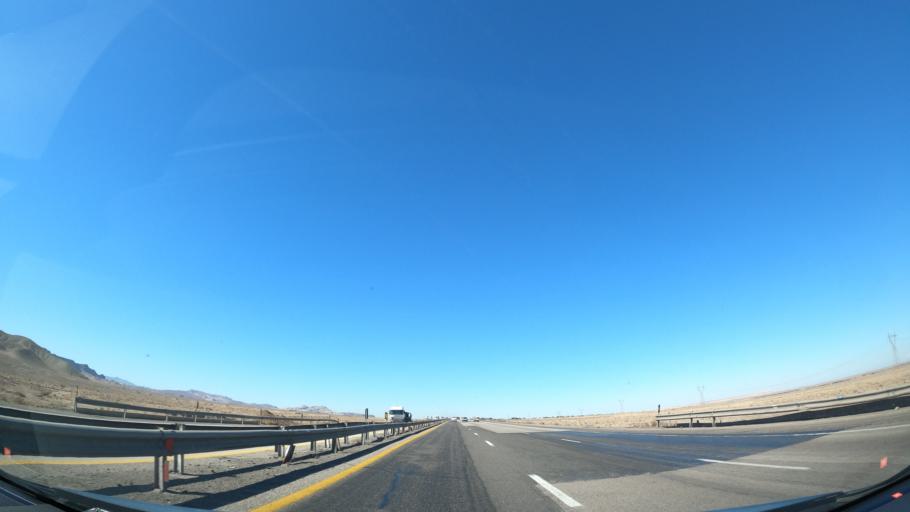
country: IR
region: Isfahan
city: Aran Bidgol
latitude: 34.3581
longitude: 51.2515
